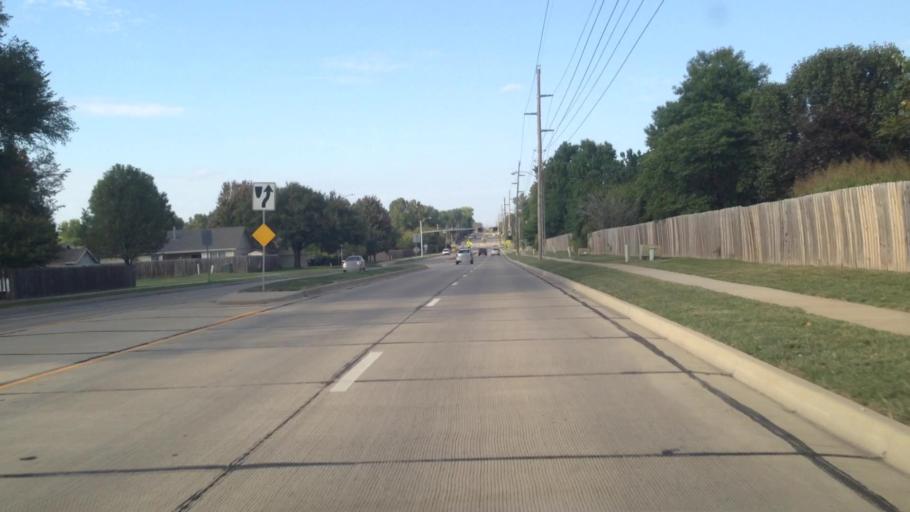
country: US
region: Kansas
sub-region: Douglas County
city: Lawrence
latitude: 38.9324
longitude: -95.2791
